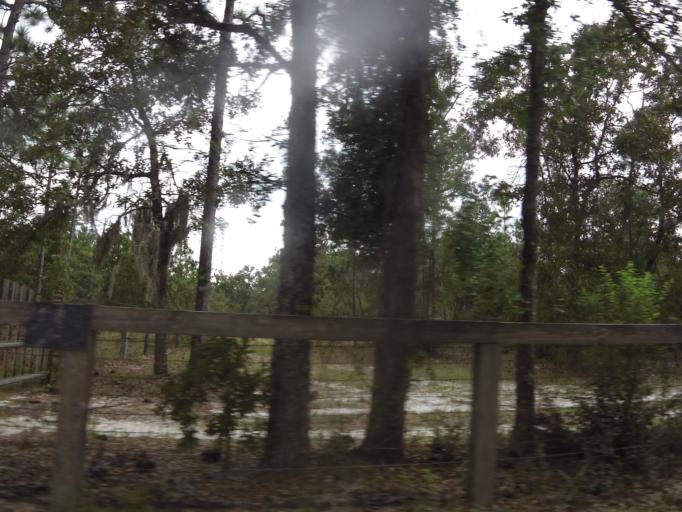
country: US
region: Florida
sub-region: Clay County
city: Middleburg
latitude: 30.1317
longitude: -81.9492
